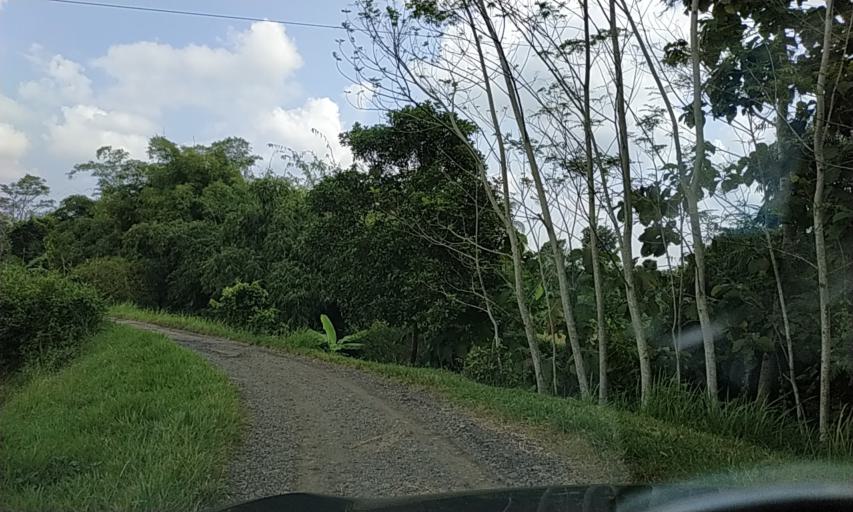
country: ID
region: Central Java
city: Bakung
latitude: -7.3382
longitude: 108.6672
